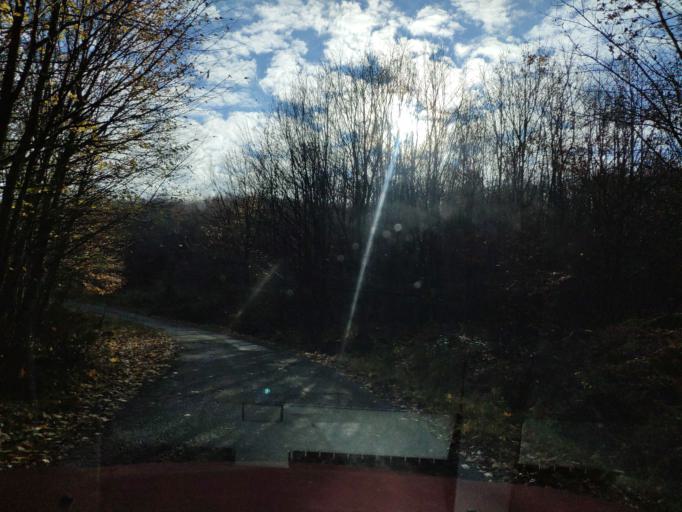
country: SK
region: Kosicky
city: Kosice
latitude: 48.6093
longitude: 21.4562
